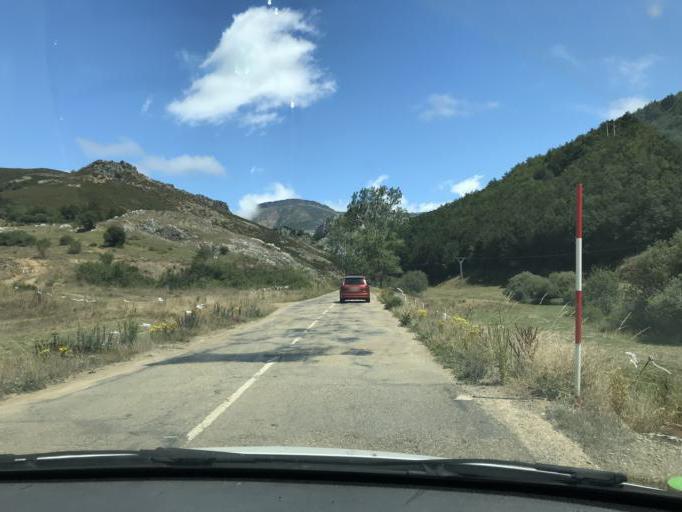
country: ES
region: Castille and Leon
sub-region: Provincia de Palencia
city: Polentinos
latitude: 43.0229
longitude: -4.4782
